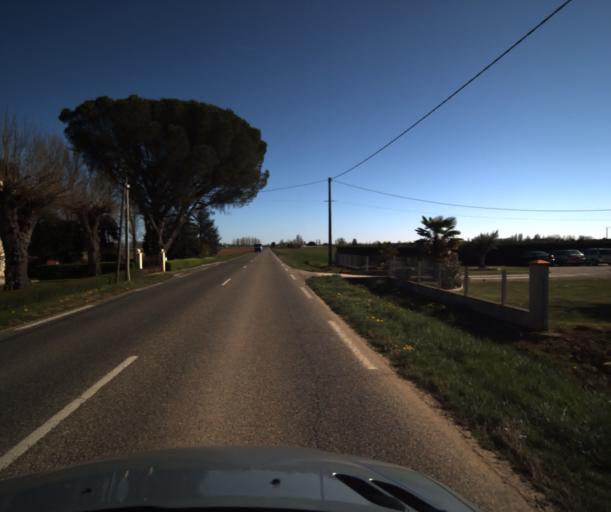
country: FR
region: Midi-Pyrenees
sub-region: Departement du Tarn-et-Garonne
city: Corbarieu
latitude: 43.9447
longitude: 1.3533
